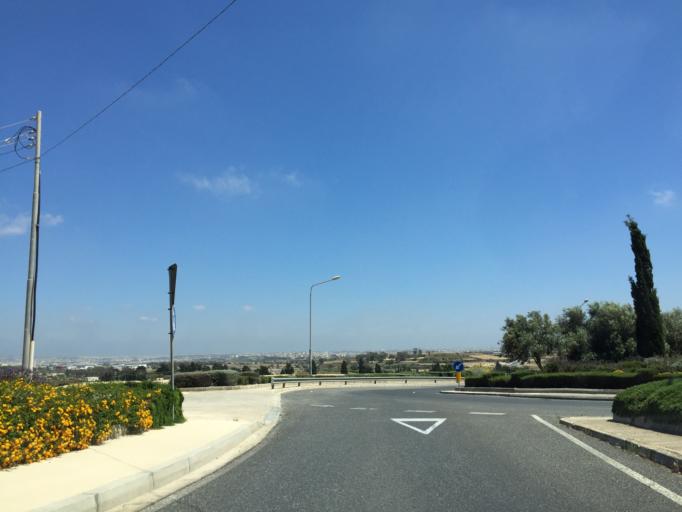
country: MT
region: L-Imdina
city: Imdina
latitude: 35.8922
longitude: 14.4046
